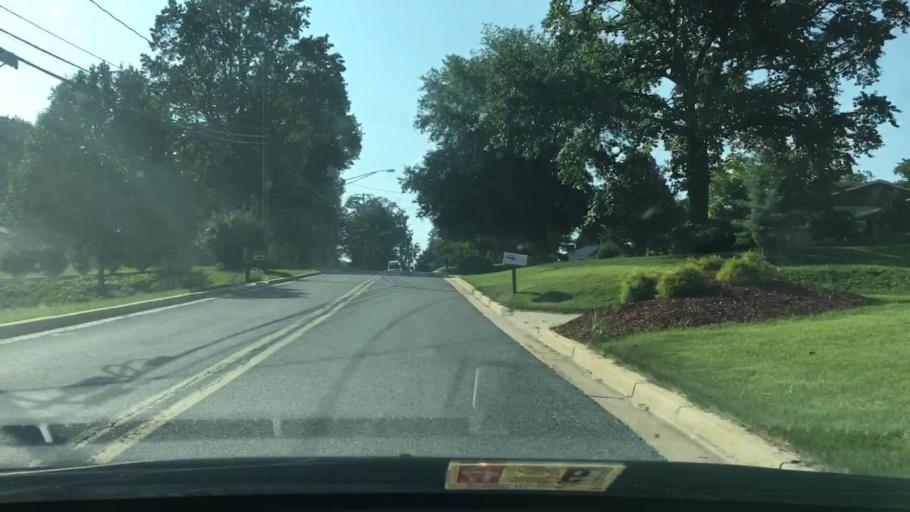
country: US
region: Maryland
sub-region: Montgomery County
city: Damascus
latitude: 39.2611
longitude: -77.2184
